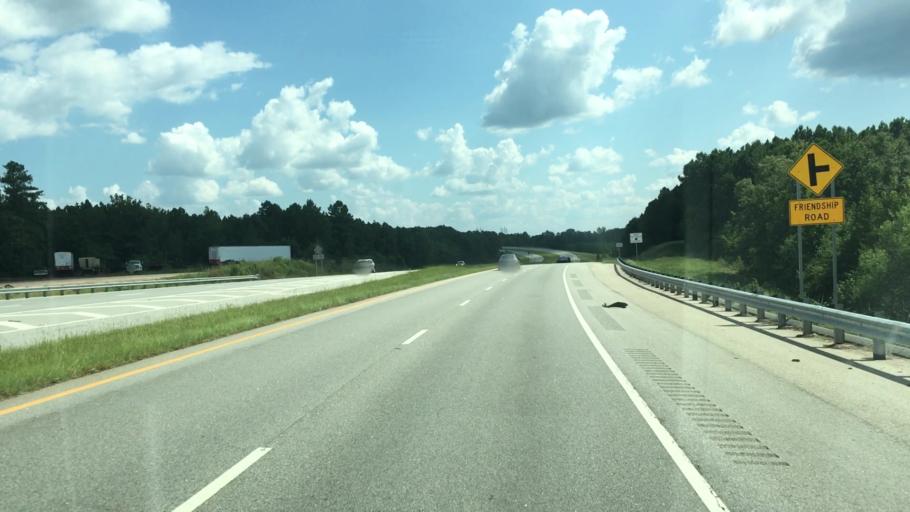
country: US
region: Georgia
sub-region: Putnam County
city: Eatonton
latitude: 33.2842
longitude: -83.3711
